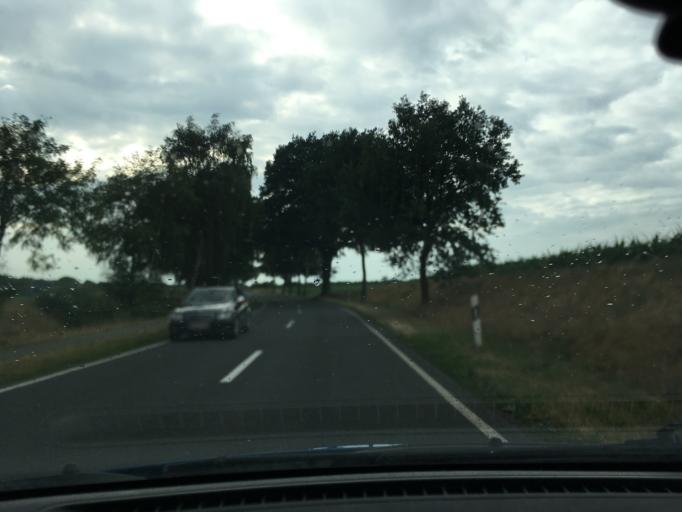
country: DE
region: Lower Saxony
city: Wenzendorf
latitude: 53.3506
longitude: 9.7473
